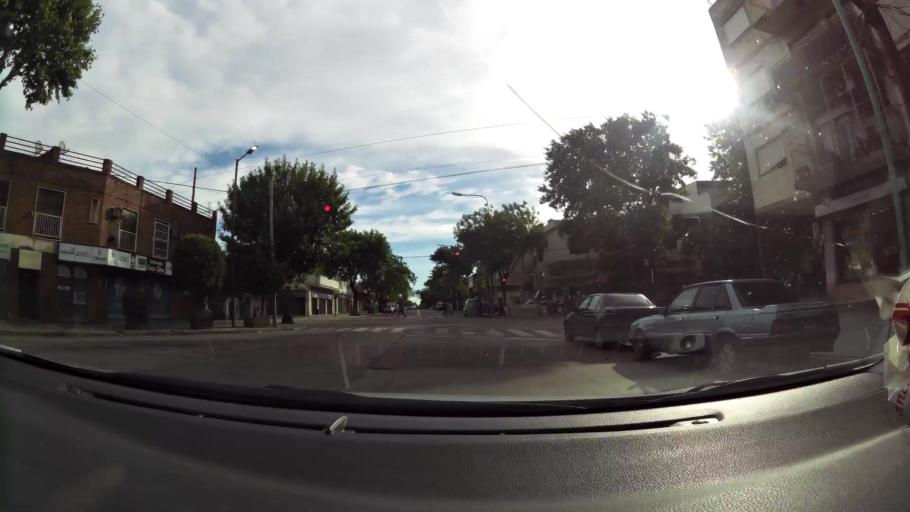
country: AR
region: Buenos Aires F.D.
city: Villa Lugano
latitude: -34.6416
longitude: -58.4429
